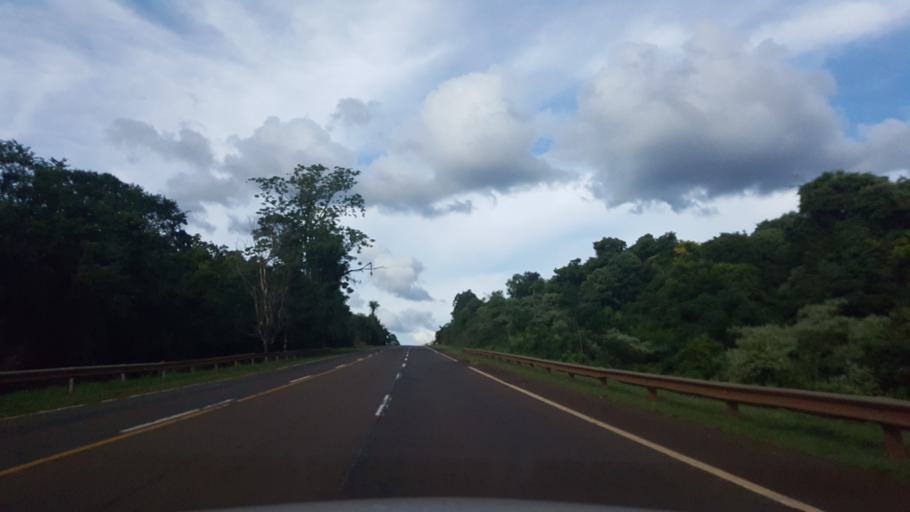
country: AR
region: Misiones
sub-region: Departamento de San Ignacio
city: San Ignacio
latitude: -27.2278
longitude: -55.5102
